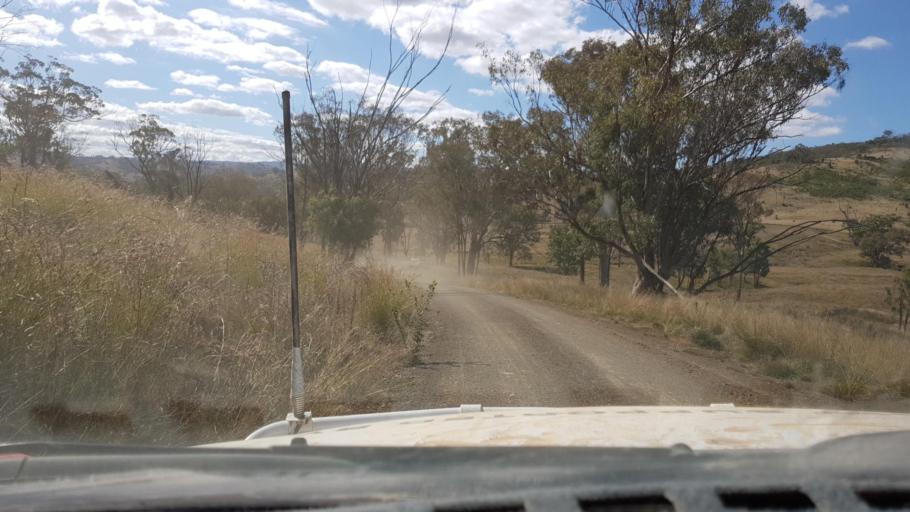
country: AU
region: New South Wales
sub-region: Tamworth Municipality
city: Manilla
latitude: -30.4682
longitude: 150.7760
